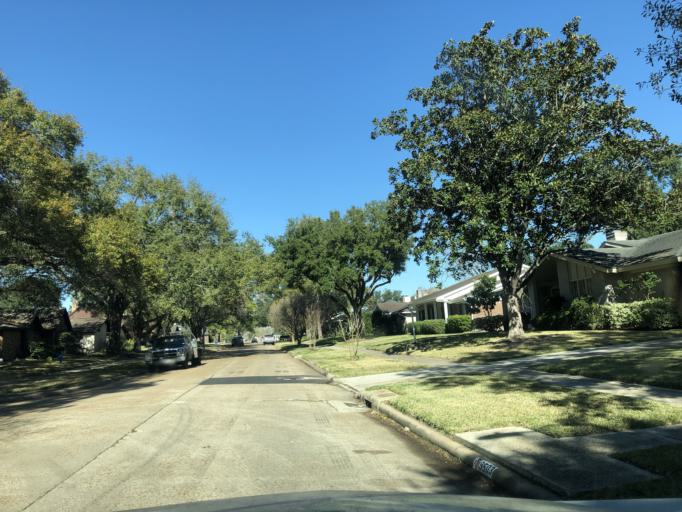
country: US
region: Texas
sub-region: Harris County
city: Bellaire
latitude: 29.6758
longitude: -95.4972
